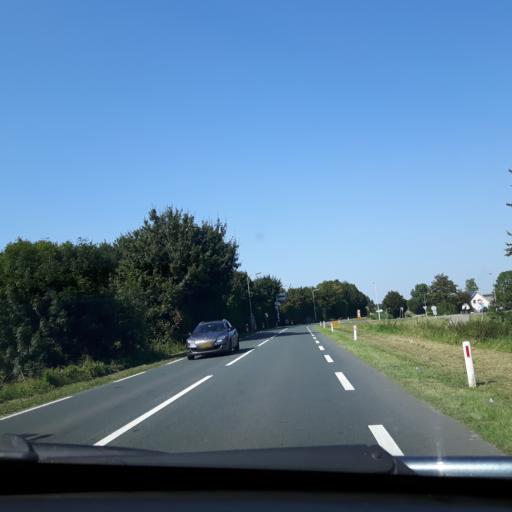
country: NL
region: Zeeland
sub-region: Gemeente Reimerswaal
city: Yerseke
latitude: 51.4800
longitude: 4.0477
